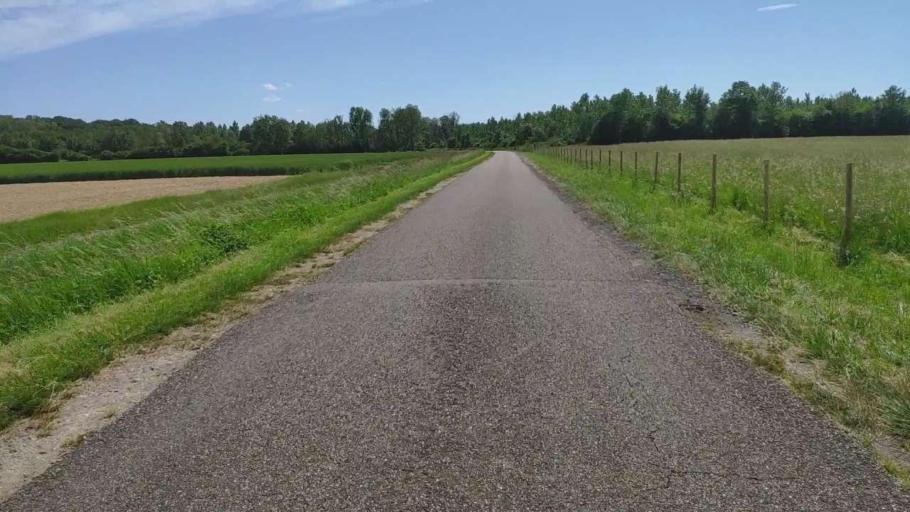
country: FR
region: Franche-Comte
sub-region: Departement du Jura
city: Bletterans
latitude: 46.7263
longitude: 5.4782
